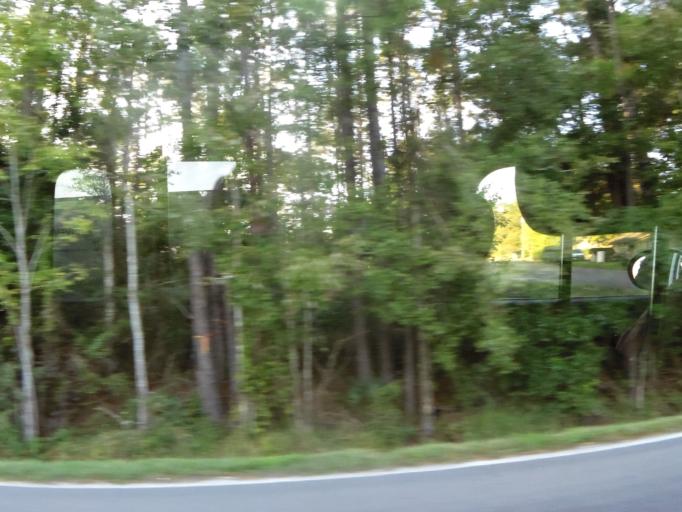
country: US
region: Florida
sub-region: Duval County
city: Jacksonville
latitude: 30.3588
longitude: -81.7647
